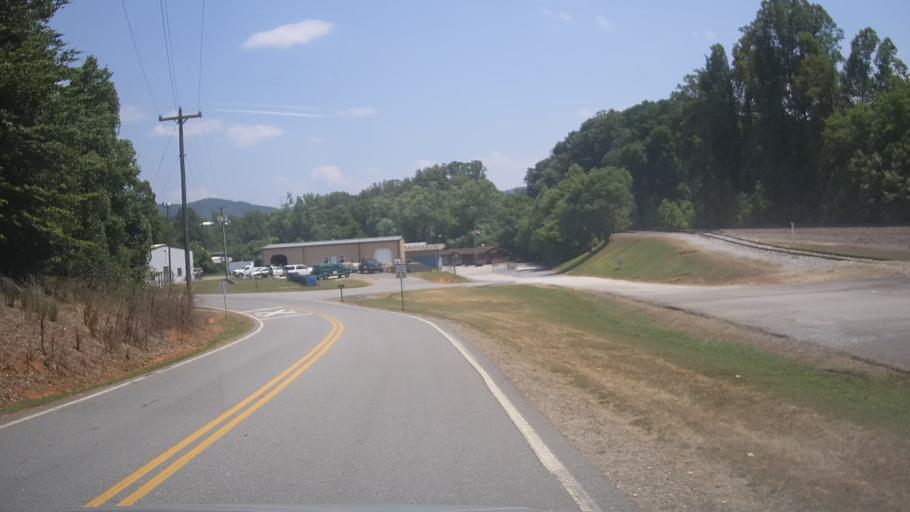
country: US
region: North Carolina
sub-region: McDowell County
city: Marion
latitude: 35.6544
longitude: -81.9620
